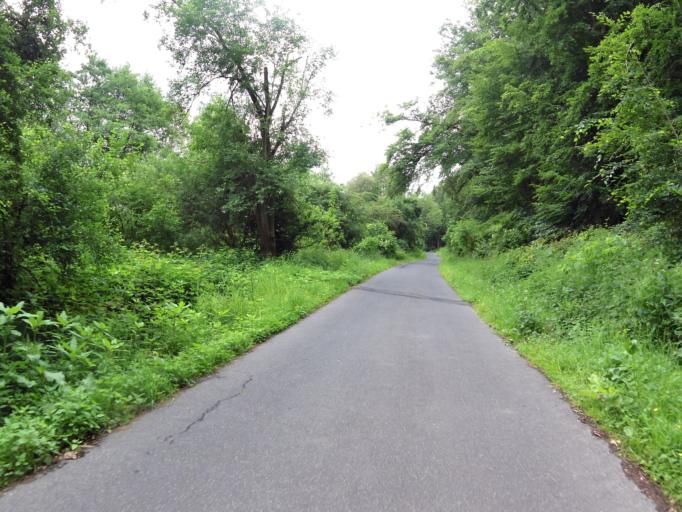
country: DE
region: Hesse
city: Breitenbach
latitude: 50.9732
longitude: 9.7661
